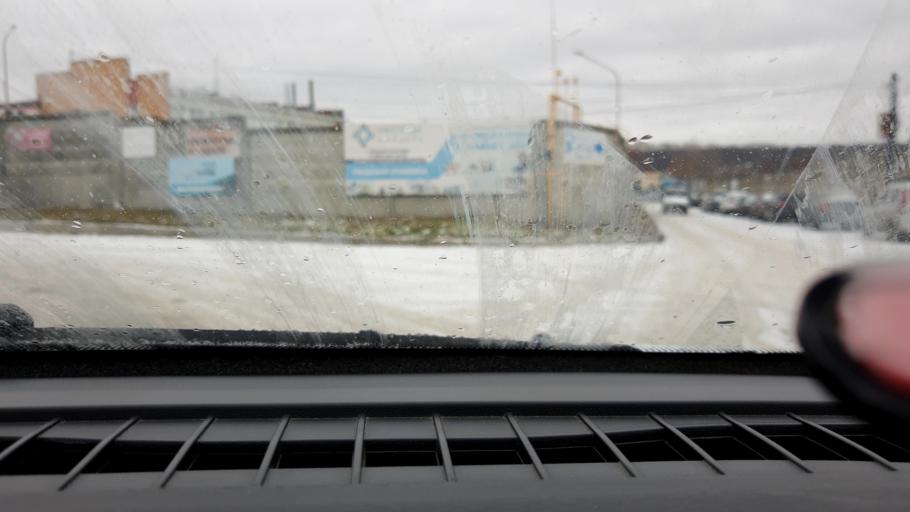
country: RU
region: Nizjnij Novgorod
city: Nizhniy Novgorod
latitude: 56.2411
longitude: 44.0024
